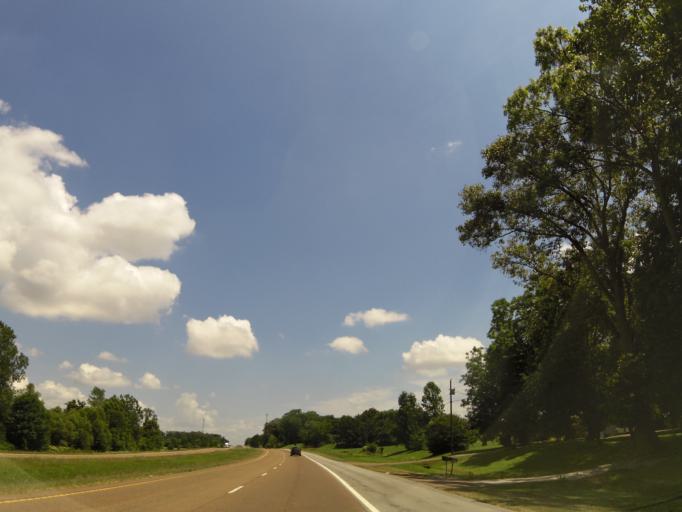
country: US
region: Tennessee
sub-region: Lauderdale County
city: Halls
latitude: 35.9184
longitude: -89.2739
